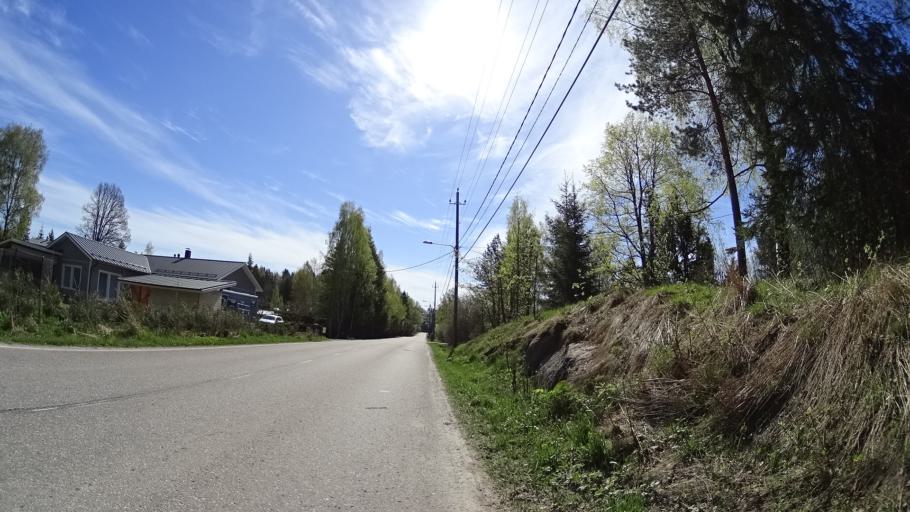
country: FI
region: Uusimaa
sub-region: Helsinki
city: Nurmijaervi
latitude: 60.3687
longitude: 24.8410
